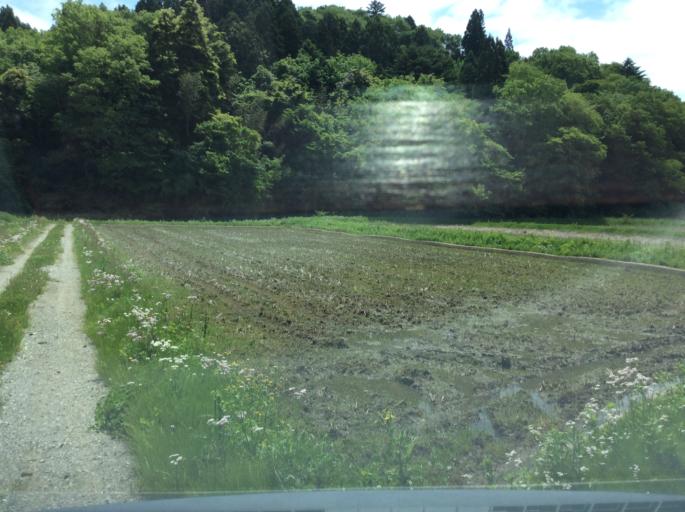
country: JP
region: Fukushima
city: Iwaki
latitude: 37.0070
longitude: 140.9455
